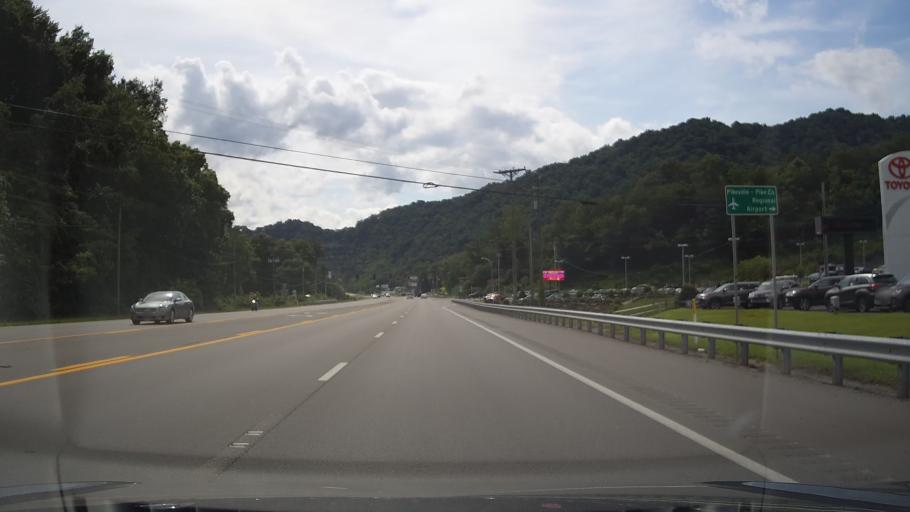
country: US
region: Kentucky
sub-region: Pike County
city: Coal Run Village
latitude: 37.5367
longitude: -82.5993
